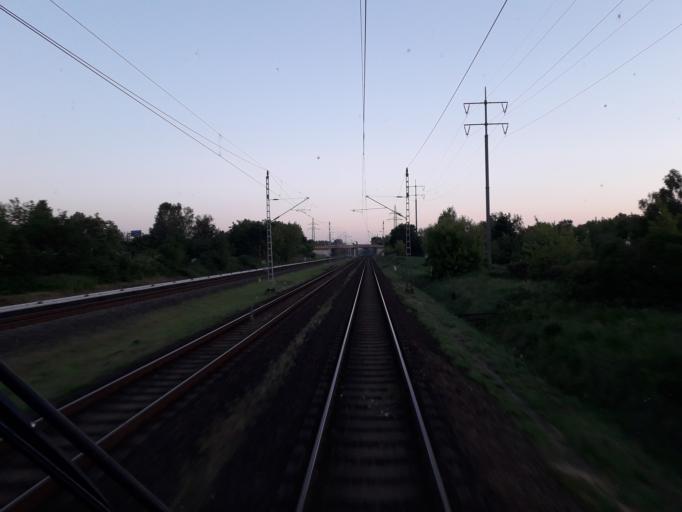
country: DE
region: Berlin
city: Buchholz
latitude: 52.6280
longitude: 13.4312
